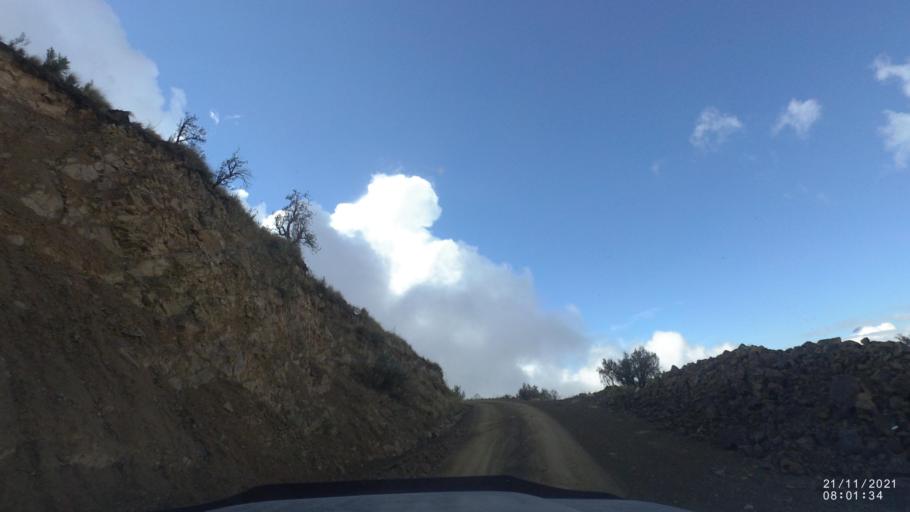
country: BO
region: Cochabamba
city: Cochabamba
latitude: -17.2868
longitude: -66.2197
